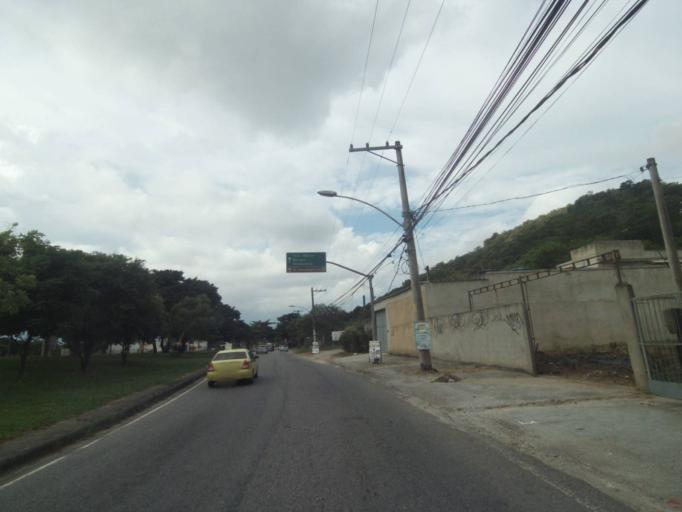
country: BR
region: Rio de Janeiro
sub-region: Nilopolis
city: Nilopolis
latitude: -22.8933
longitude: -43.3953
